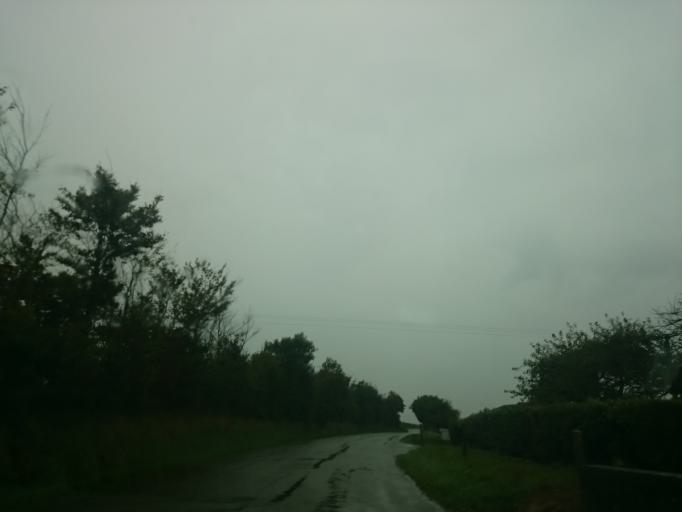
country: FR
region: Brittany
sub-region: Departement du Finistere
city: Le Drennec
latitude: 48.5387
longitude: -4.3789
